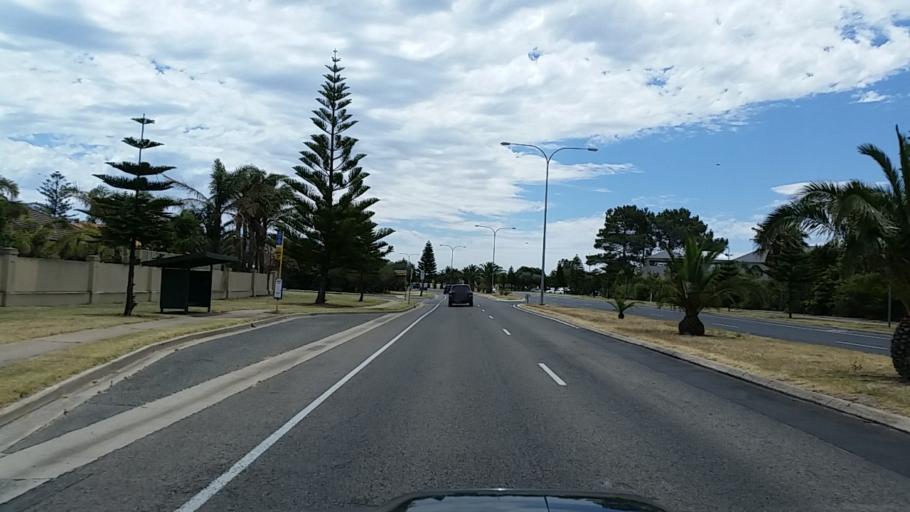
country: AU
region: South Australia
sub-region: Charles Sturt
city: West Lakes Shore
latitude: -34.8783
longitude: 138.4849
